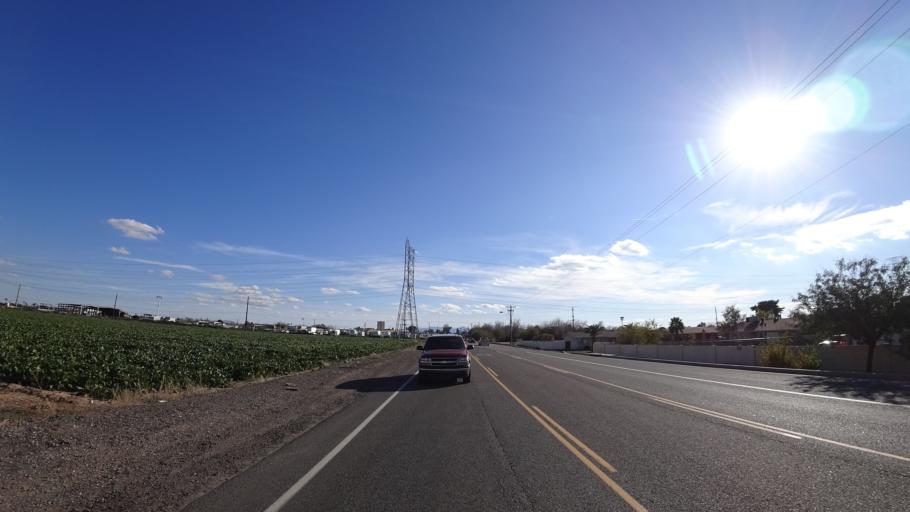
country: US
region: Arizona
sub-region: Maricopa County
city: Peoria
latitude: 33.5573
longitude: -112.2378
